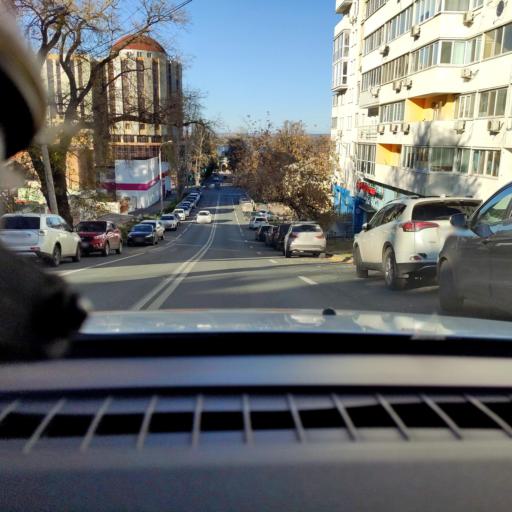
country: RU
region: Samara
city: Rozhdestveno
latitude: 53.1842
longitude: 50.0817
